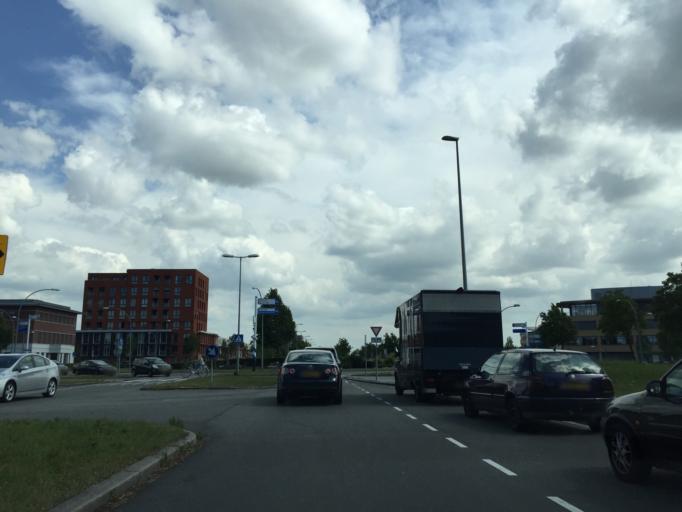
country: NL
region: South Holland
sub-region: Gemeente Rijnwoude
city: Benthuizen
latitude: 52.0617
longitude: 4.5285
